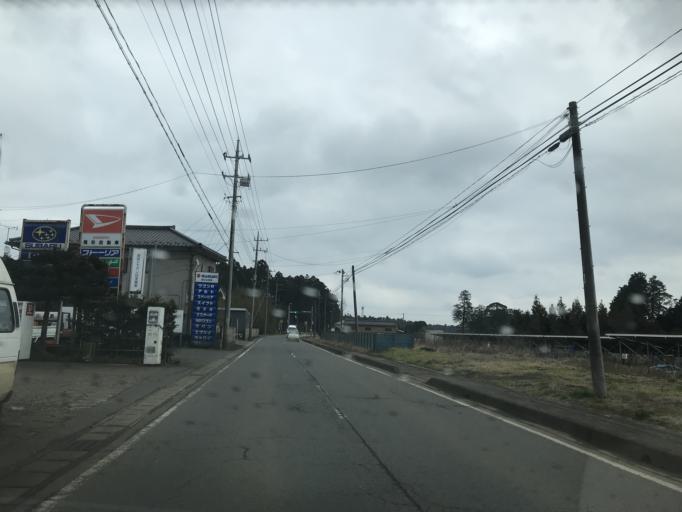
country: JP
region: Chiba
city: Sawara
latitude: 35.8473
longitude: 140.5163
